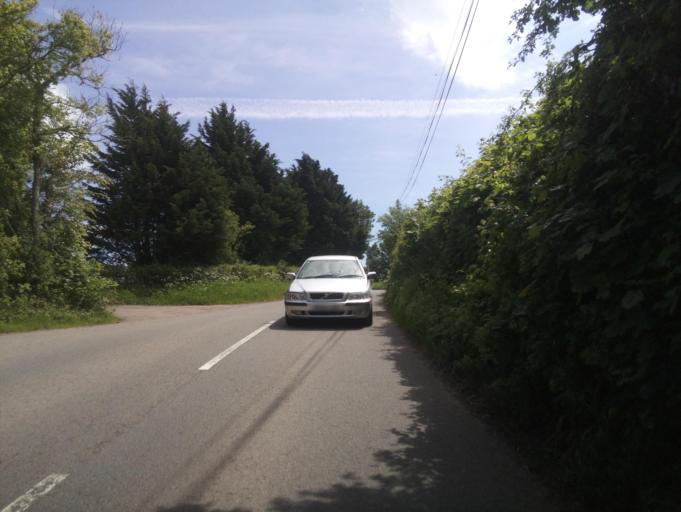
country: GB
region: England
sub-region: Herefordshire
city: Llanrothal
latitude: 51.8581
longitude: -2.8076
